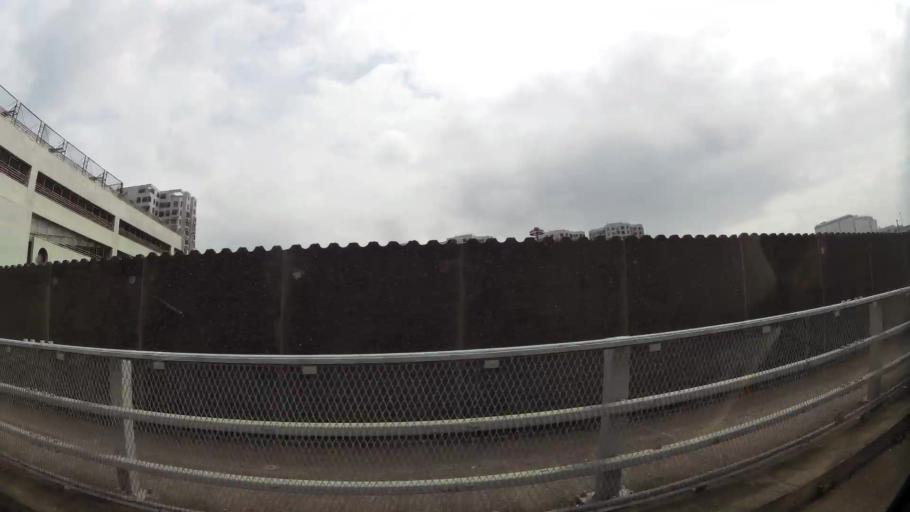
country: HK
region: Wanchai
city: Wan Chai
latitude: 22.2747
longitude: 114.2393
